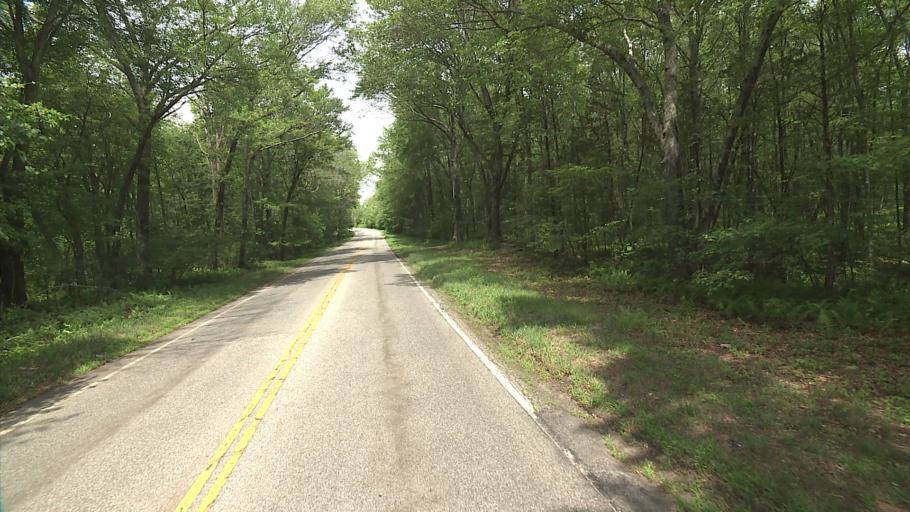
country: US
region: Connecticut
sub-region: New London County
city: Jewett City
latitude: 41.5701
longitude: -71.9694
